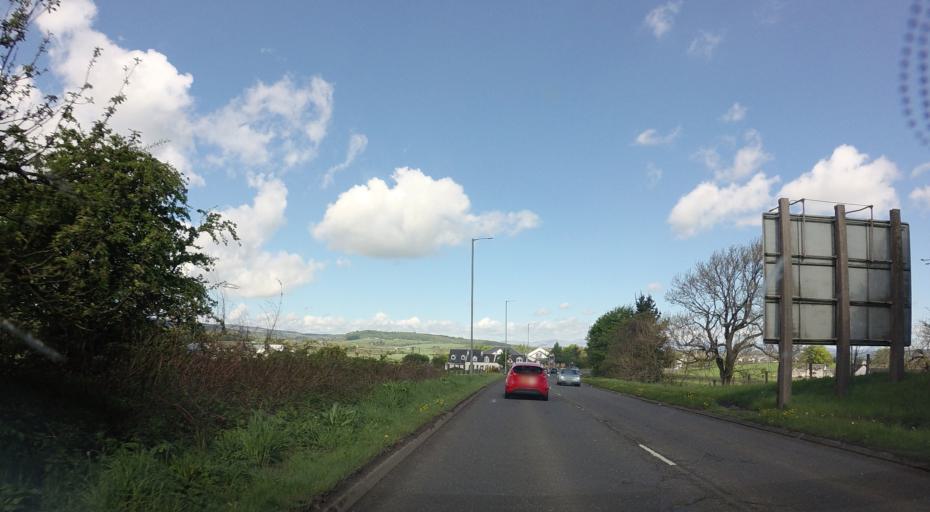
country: GB
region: Scotland
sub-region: Stirling
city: Bannockburn
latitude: 56.0798
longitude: -3.9226
